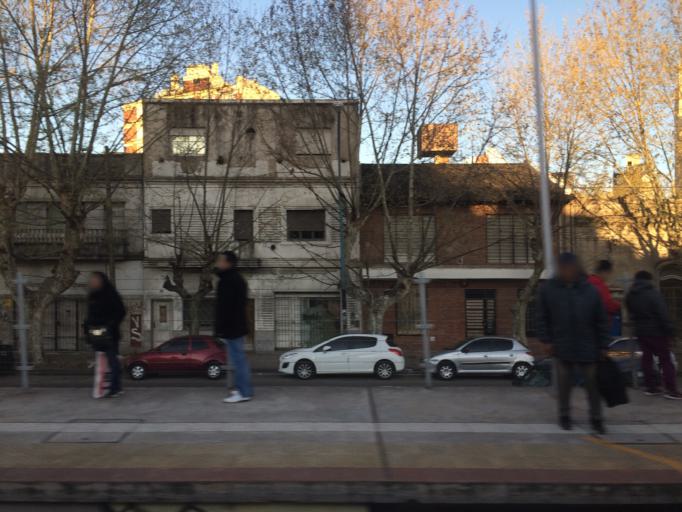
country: AR
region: Buenos Aires
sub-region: Partido de Lanus
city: Lanus
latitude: -34.7097
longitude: -58.3912
